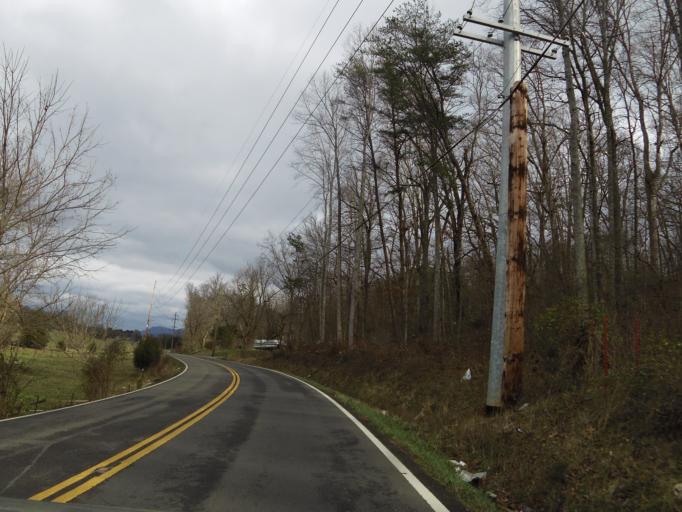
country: US
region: Tennessee
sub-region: Union County
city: Condon
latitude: 36.1267
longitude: -83.8356
